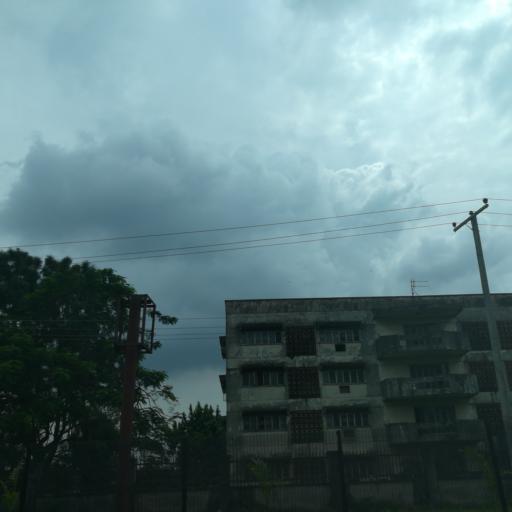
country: NG
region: Rivers
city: Port Harcourt
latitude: 4.8283
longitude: 7.0031
